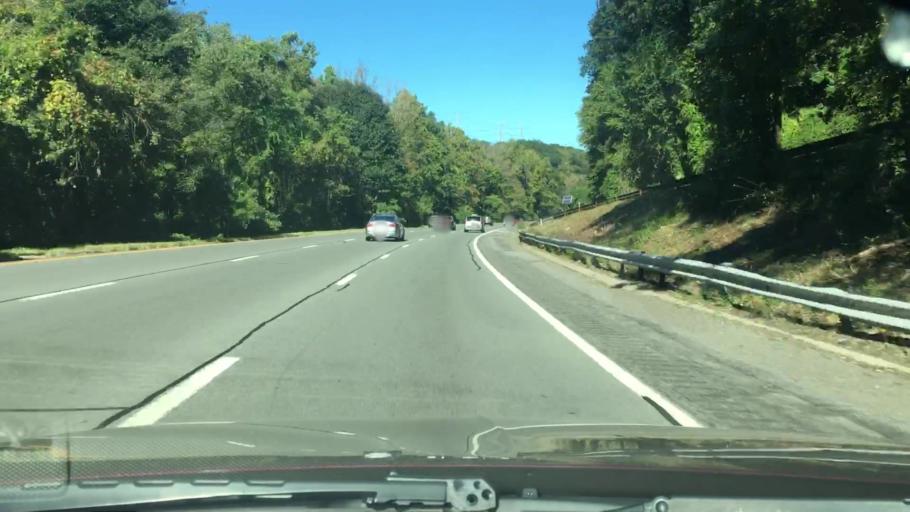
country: US
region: New York
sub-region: Westchester County
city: Greenville
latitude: 40.9896
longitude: -73.8388
